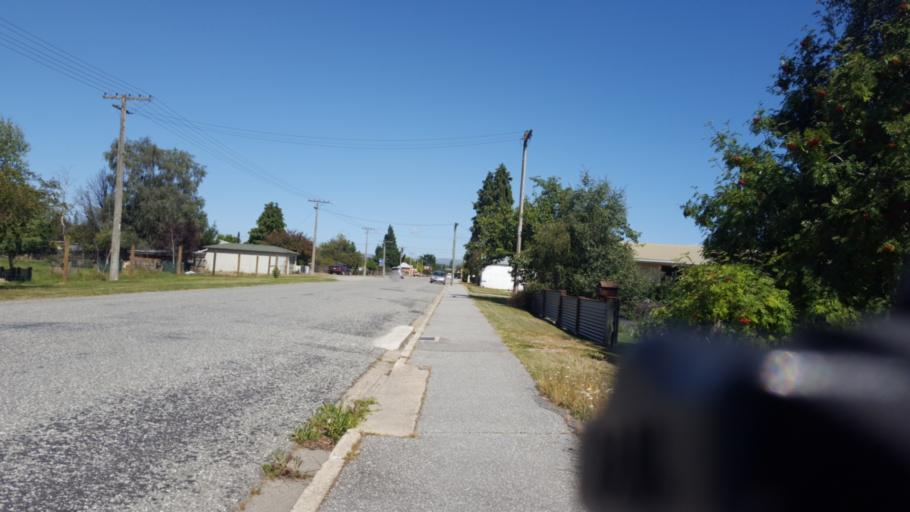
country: NZ
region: Otago
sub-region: Dunedin City
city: Dunedin
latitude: -45.1303
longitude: 170.1049
